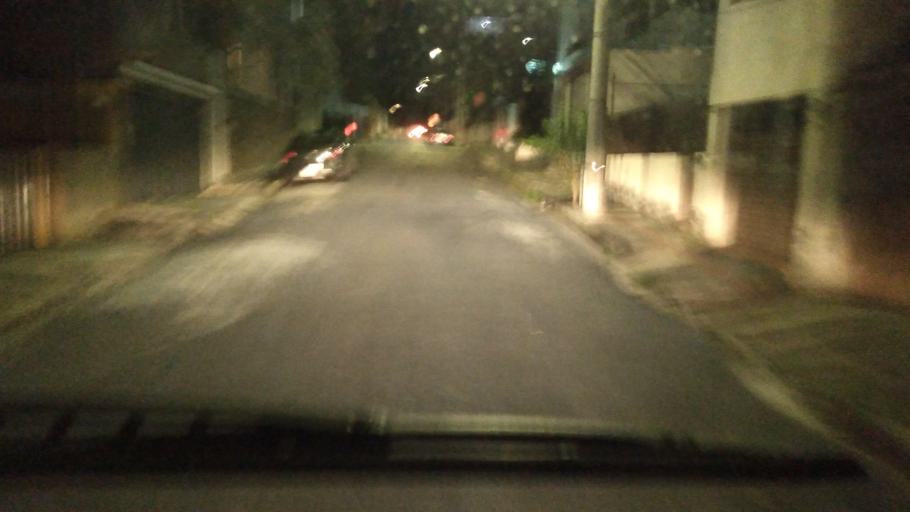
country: BR
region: Minas Gerais
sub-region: Belo Horizonte
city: Belo Horizonte
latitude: -19.9119
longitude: -43.9590
